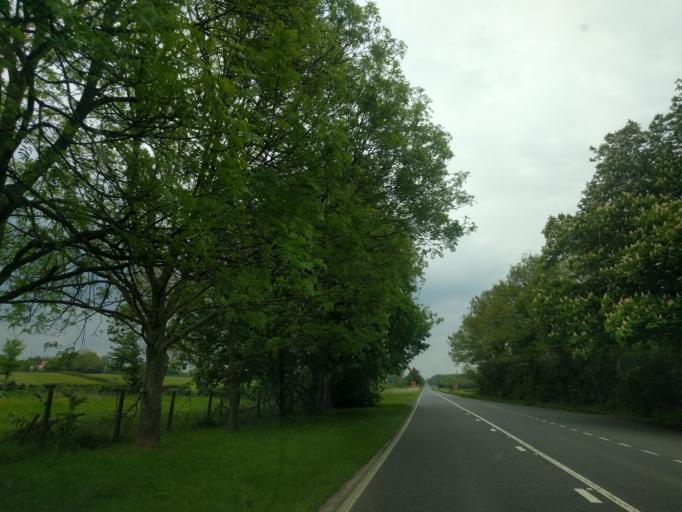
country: GB
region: England
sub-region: Somerset
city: Castle Cary
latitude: 51.0835
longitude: -2.6128
